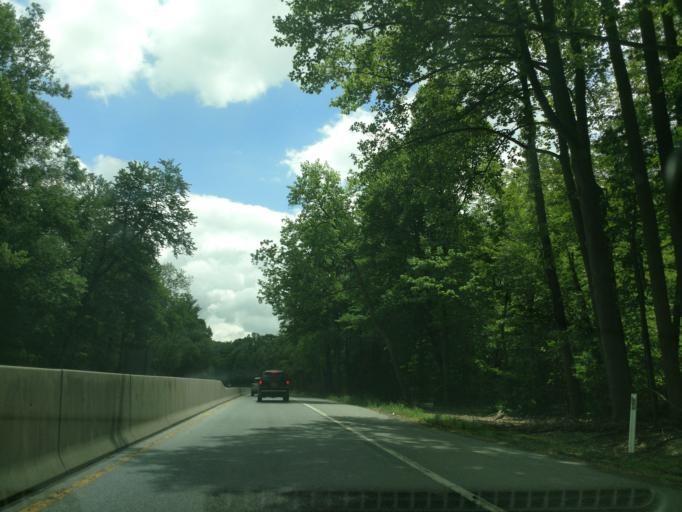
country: US
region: Pennsylvania
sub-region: Lebanon County
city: Cornwall
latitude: 40.2597
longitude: -76.4321
